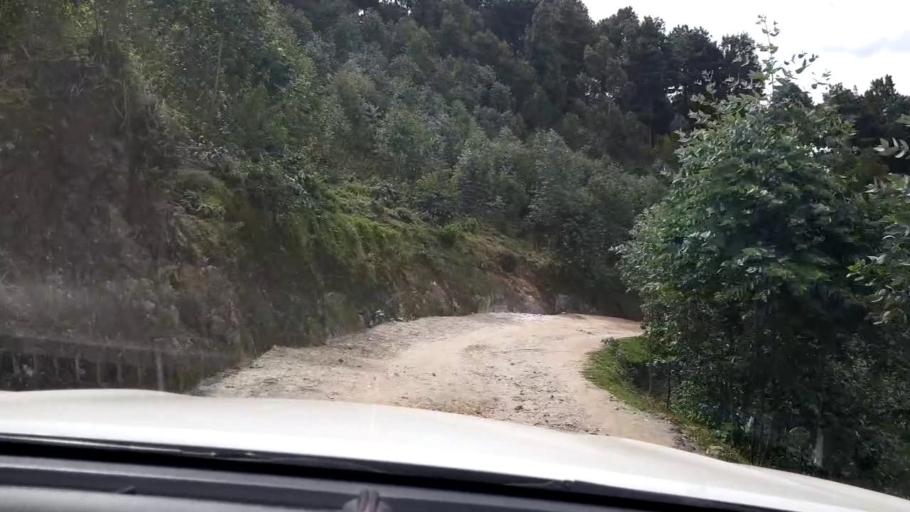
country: RW
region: Western Province
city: Kibuye
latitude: -1.8754
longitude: 29.4530
